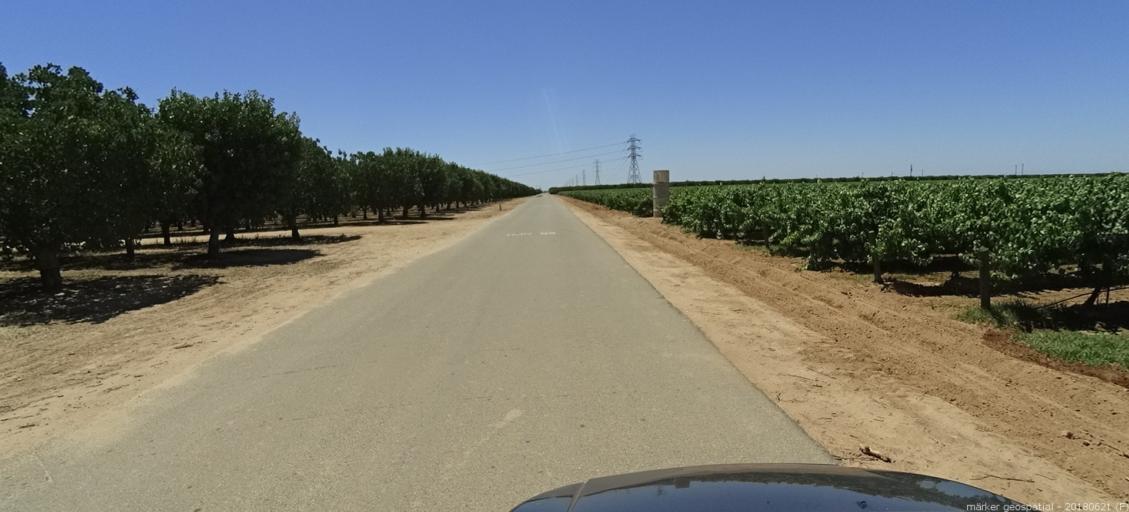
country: US
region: California
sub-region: Madera County
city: Bonadelle Ranchos-Madera Ranchos
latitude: 36.9201
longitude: -119.9124
